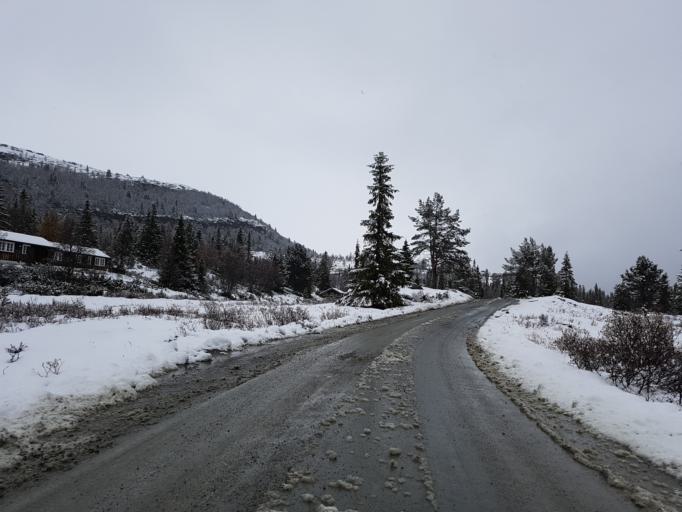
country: NO
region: Oppland
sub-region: Sel
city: Otta
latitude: 61.8050
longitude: 9.6936
